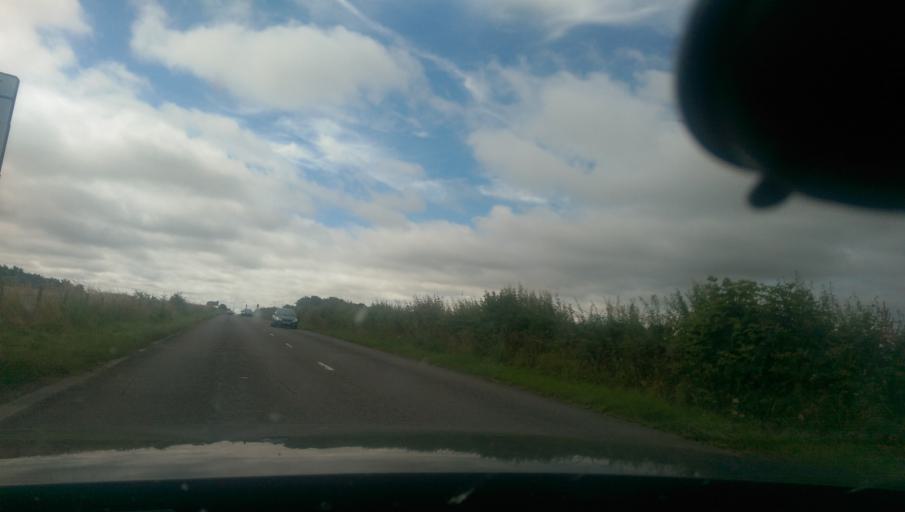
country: GB
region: England
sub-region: Wiltshire
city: Winterbourne Stoke
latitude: 51.1756
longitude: -1.8593
